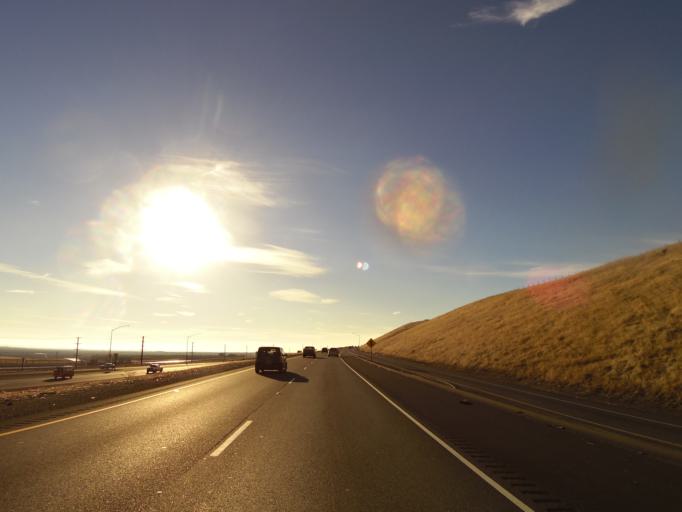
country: US
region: California
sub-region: Stanislaus County
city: Patterson
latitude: 37.4629
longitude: -121.1799
